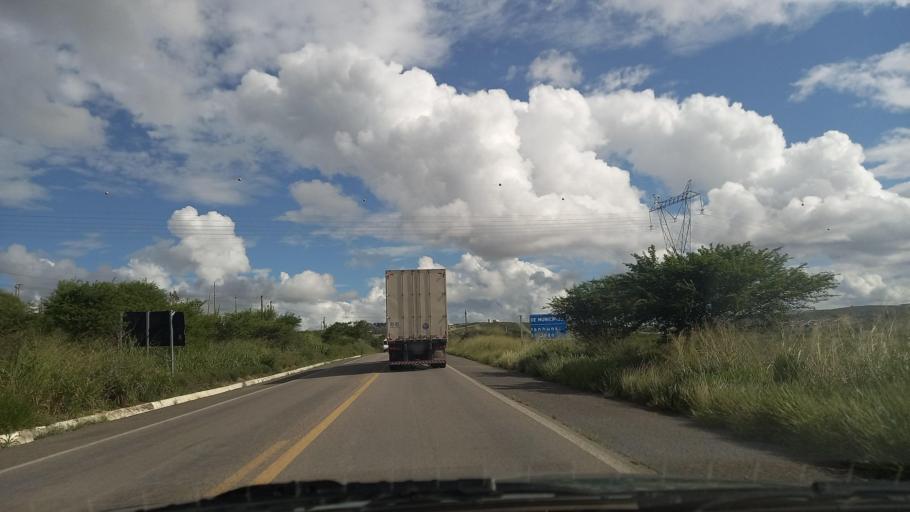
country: BR
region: Pernambuco
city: Garanhuns
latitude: -8.8488
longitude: -36.4608
